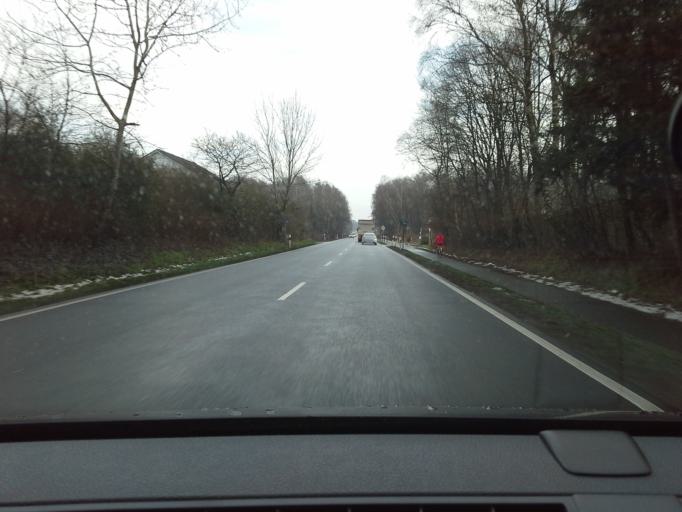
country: DE
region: Schleswig-Holstein
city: Henstedt-Ulzburg
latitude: 53.7454
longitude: 10.0083
